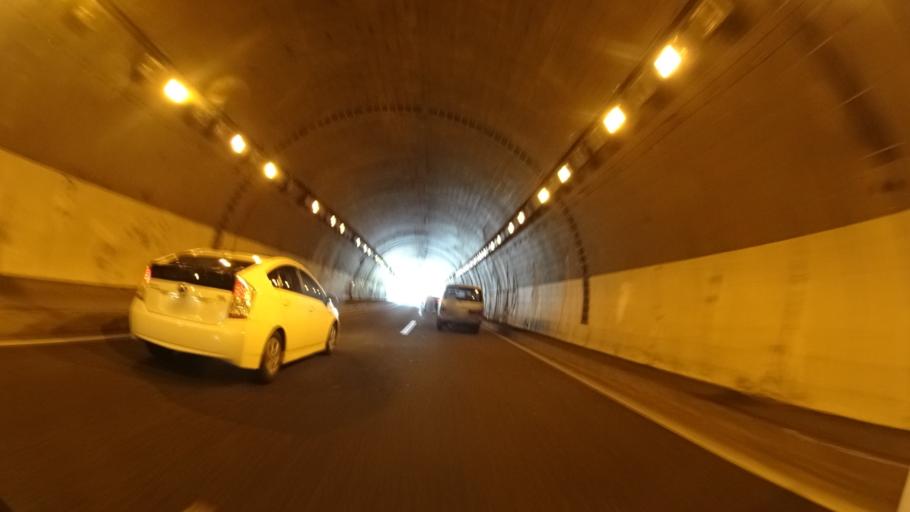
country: JP
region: Ehime
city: Kawanoecho
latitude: 33.9652
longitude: 133.5392
